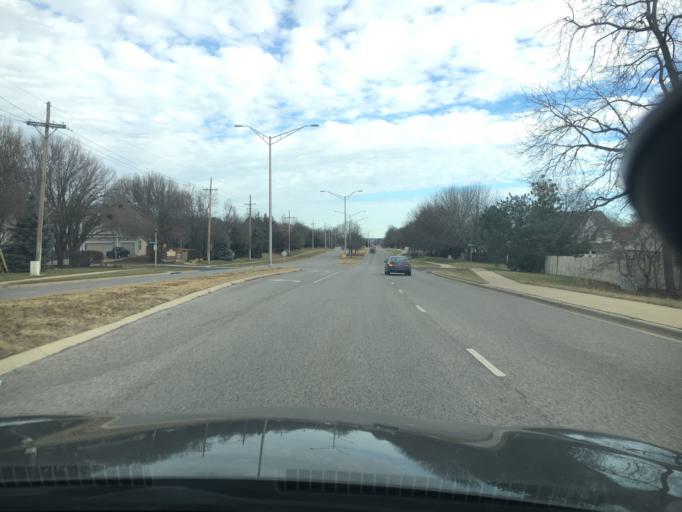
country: US
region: Kansas
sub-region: Johnson County
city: Leawood
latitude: 38.8546
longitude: -94.6591
